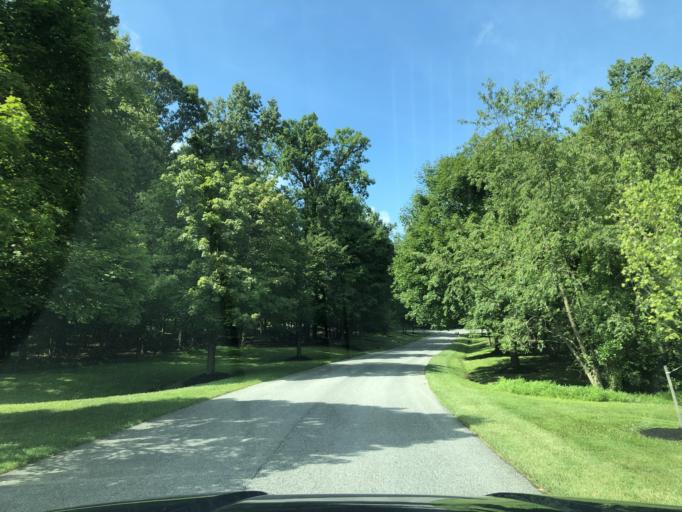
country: US
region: Maryland
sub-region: Howard County
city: Highland
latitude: 39.2080
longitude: -76.9750
